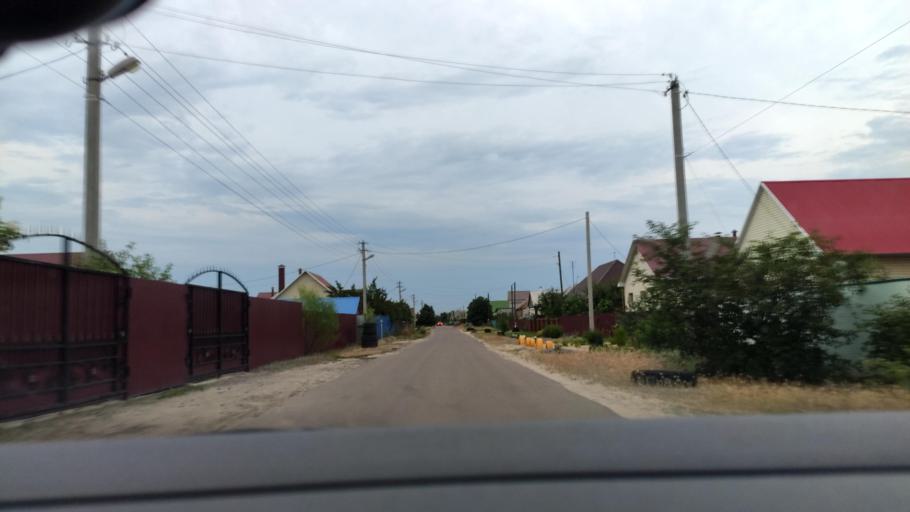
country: RU
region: Voronezj
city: Maslovka
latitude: 51.5698
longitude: 39.2504
